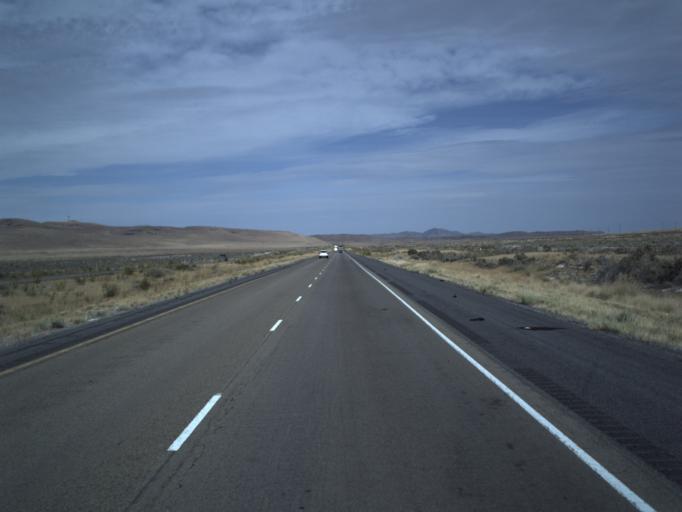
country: US
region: Utah
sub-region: Tooele County
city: Grantsville
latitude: 40.7791
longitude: -112.8107
